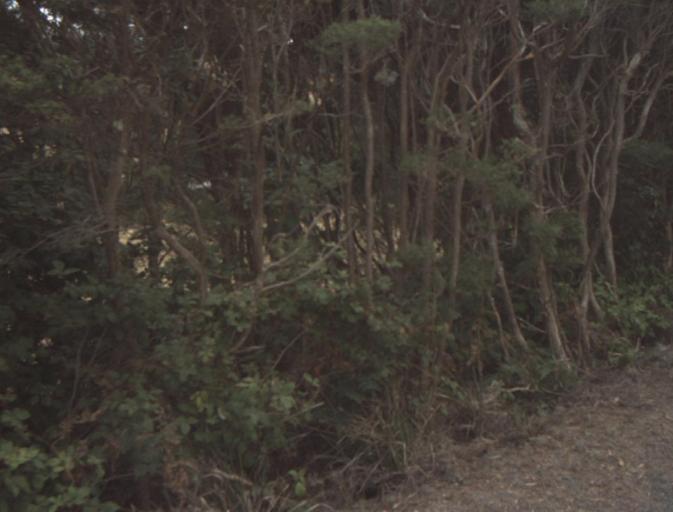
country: AU
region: Tasmania
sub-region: Launceston
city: Mayfield
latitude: -41.2995
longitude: 147.0320
